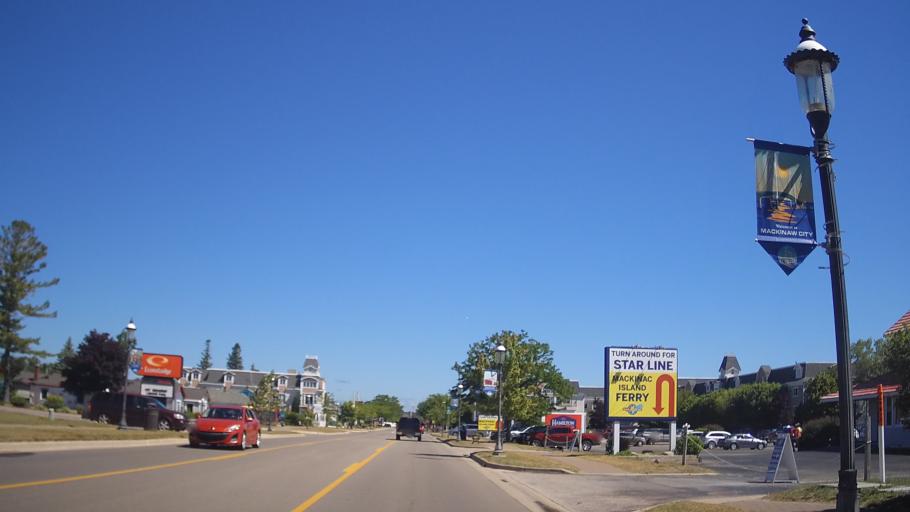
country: US
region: Michigan
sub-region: Mackinac County
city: Saint Ignace
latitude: 45.7735
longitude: -84.7267
